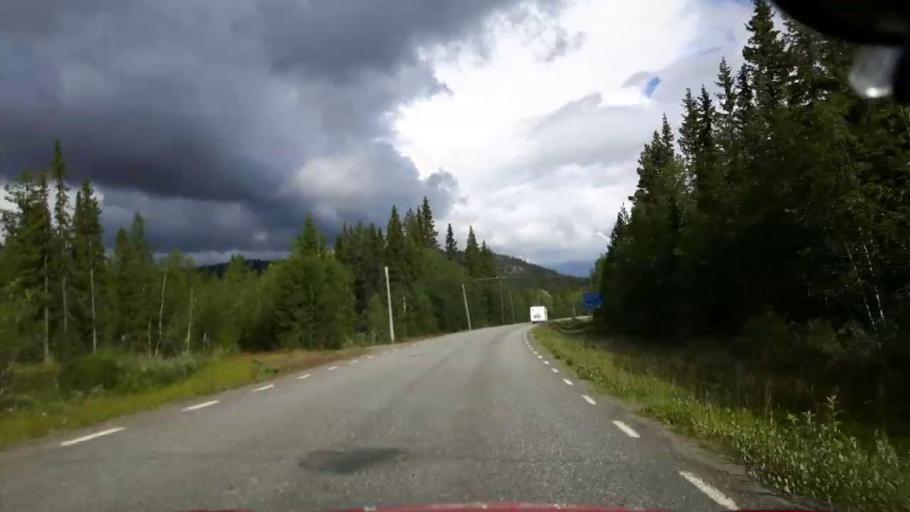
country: SE
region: Vaesterbotten
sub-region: Vilhelmina Kommun
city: Sjoberg
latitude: 64.9330
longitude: 15.8586
